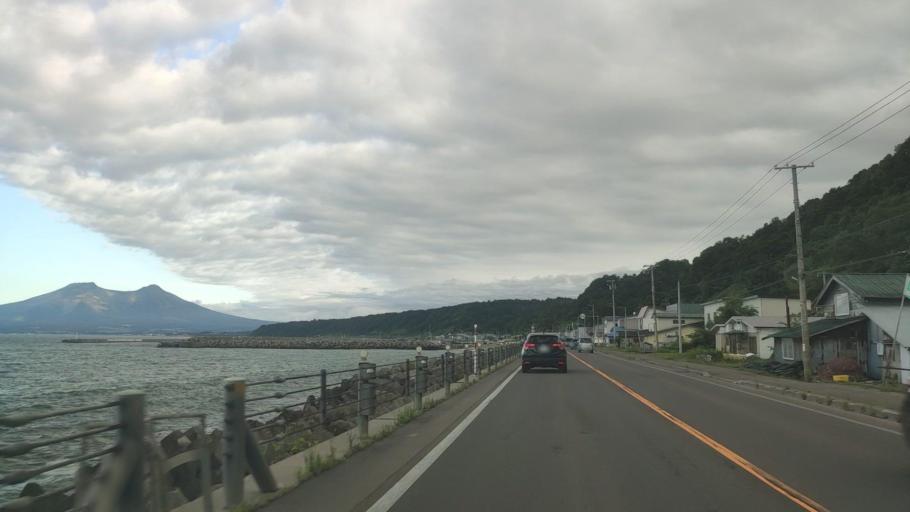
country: JP
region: Hokkaido
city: Nanae
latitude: 42.1384
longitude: 140.5053
